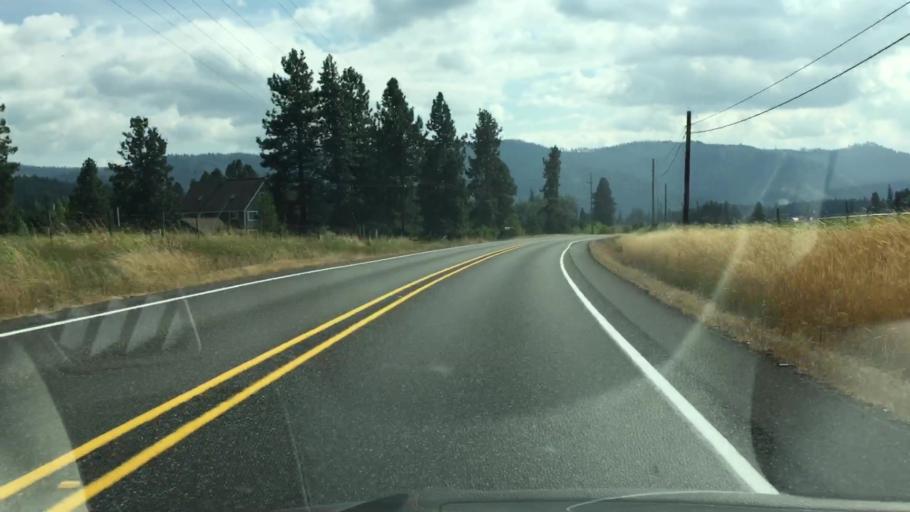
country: US
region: Washington
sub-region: Klickitat County
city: White Salmon
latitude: 45.8196
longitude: -121.4881
